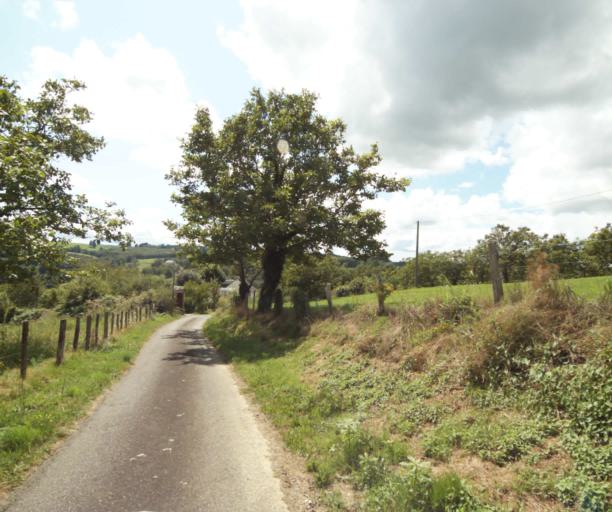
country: FR
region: Limousin
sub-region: Departement de la Correze
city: Sainte-Fortunade
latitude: 45.1715
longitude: 1.8271
